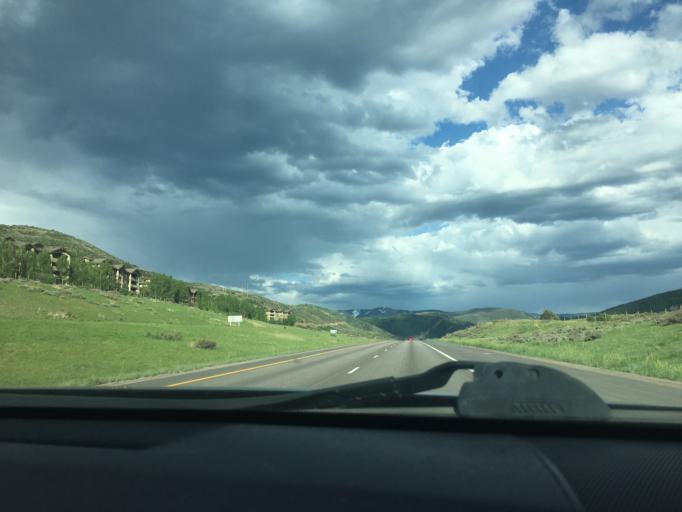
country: US
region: Colorado
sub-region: Eagle County
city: Avon
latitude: 39.6323
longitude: -106.5093
